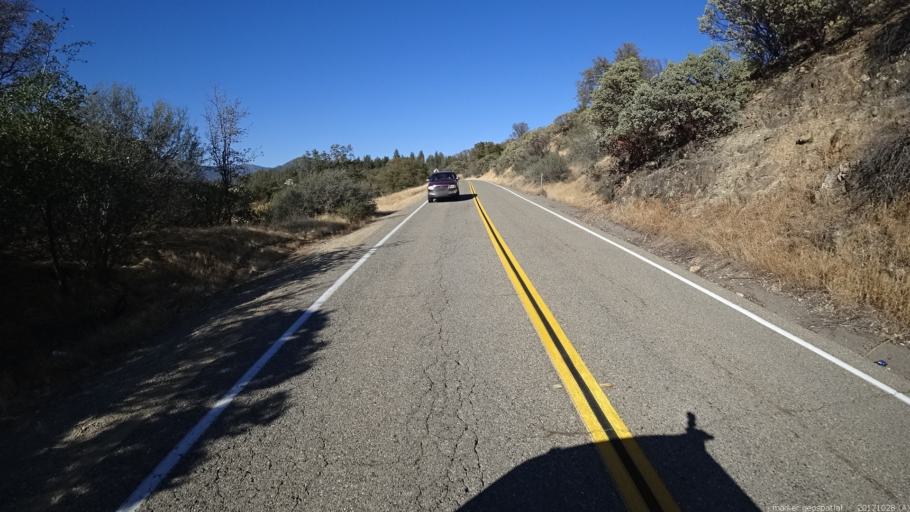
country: US
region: California
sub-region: Shasta County
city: Shasta
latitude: 40.6116
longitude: -122.4541
